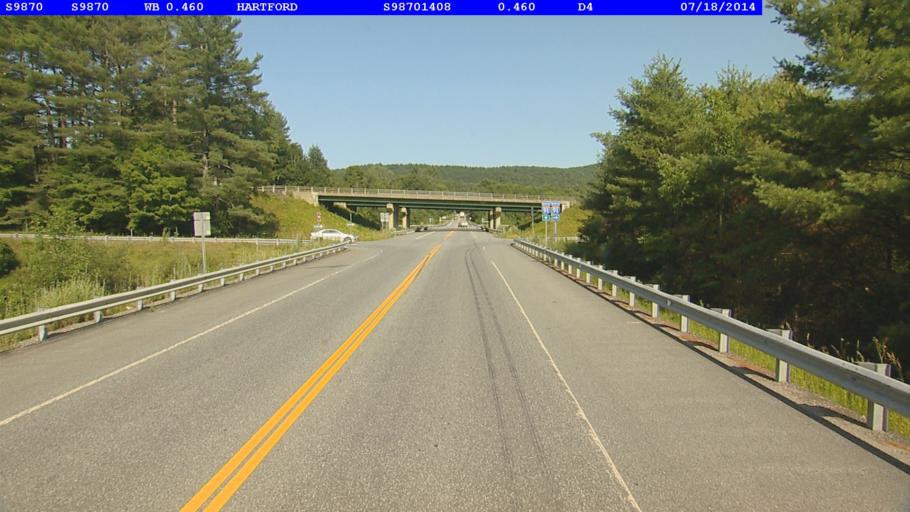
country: US
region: Vermont
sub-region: Windsor County
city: Wilder
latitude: 43.6659
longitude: -72.3176
